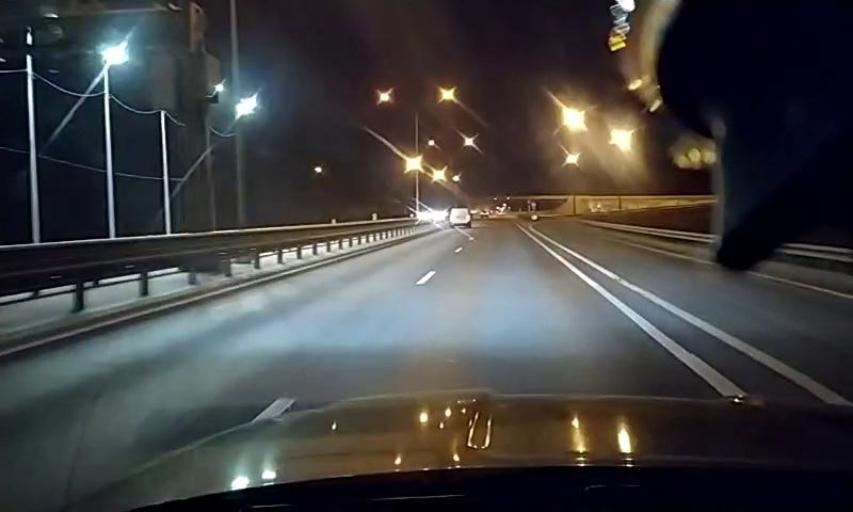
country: RU
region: Leningrad
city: Agalatovo
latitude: 60.2248
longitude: 30.3583
